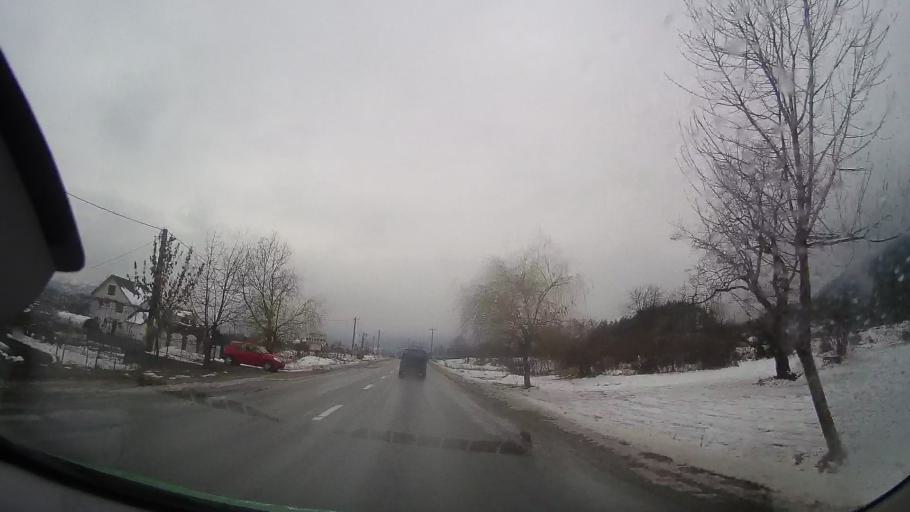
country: RO
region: Neamt
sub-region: Comuna Pangarati
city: Stejaru
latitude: 46.9252
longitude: 26.1917
